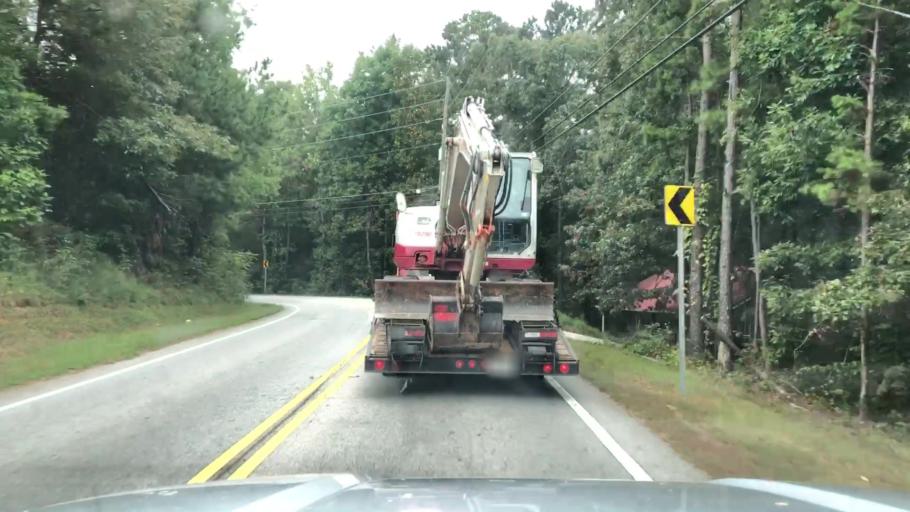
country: US
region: Georgia
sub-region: Bartow County
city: Emerson
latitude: 34.0487
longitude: -84.7777
